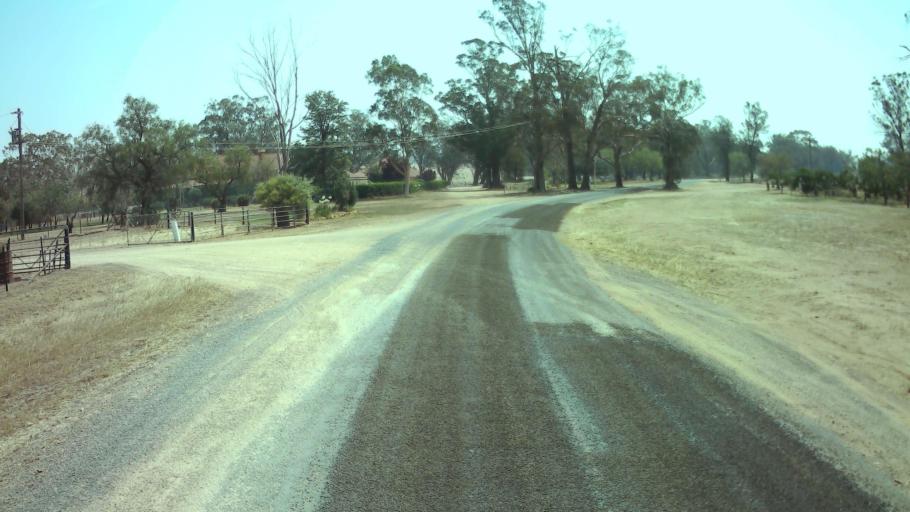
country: AU
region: New South Wales
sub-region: Weddin
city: Grenfell
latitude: -33.6437
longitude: 148.2564
